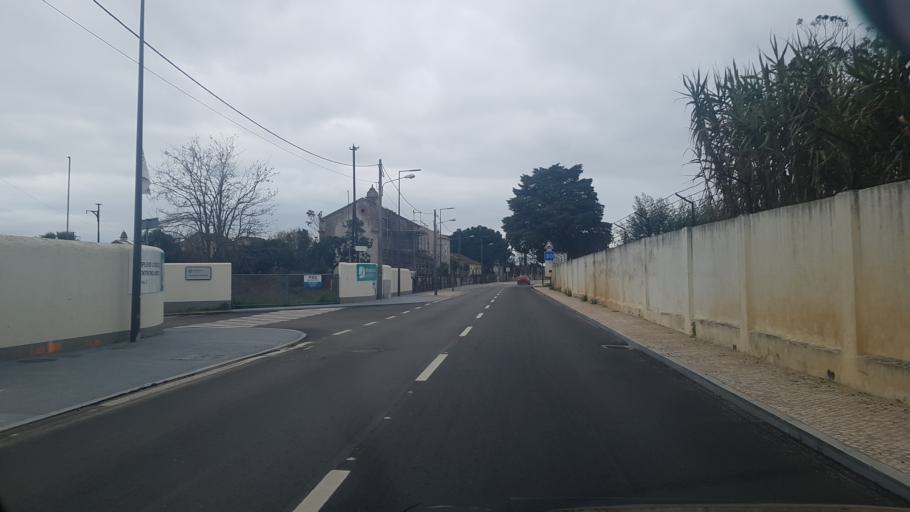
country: PT
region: Santarem
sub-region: Entroncamento
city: Entroncamento
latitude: 39.4605
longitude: -8.4817
